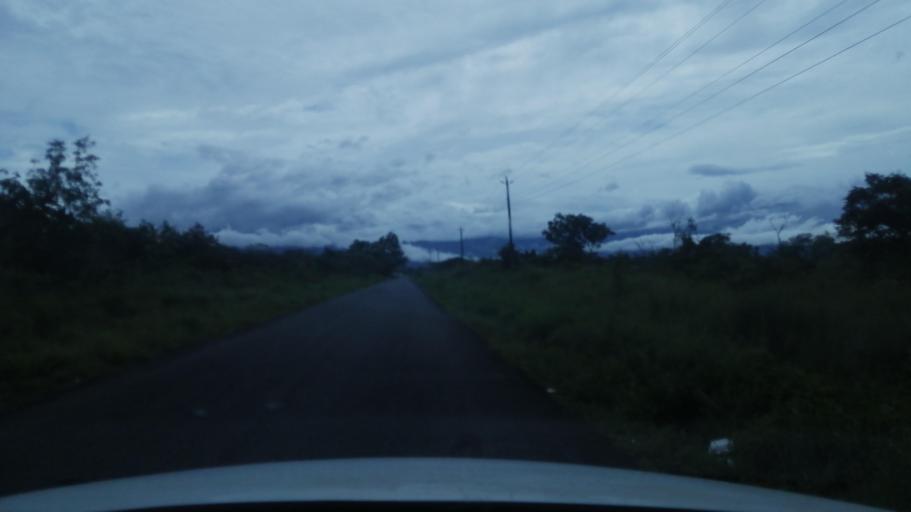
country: PA
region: Chiriqui
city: Potrerillos Abajo
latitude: 8.6696
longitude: -82.4424
